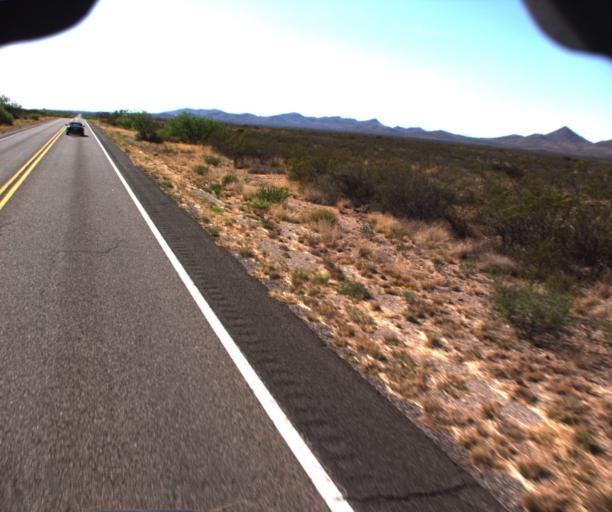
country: US
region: Arizona
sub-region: Cochise County
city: Tombstone
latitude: 31.7690
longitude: -110.1225
